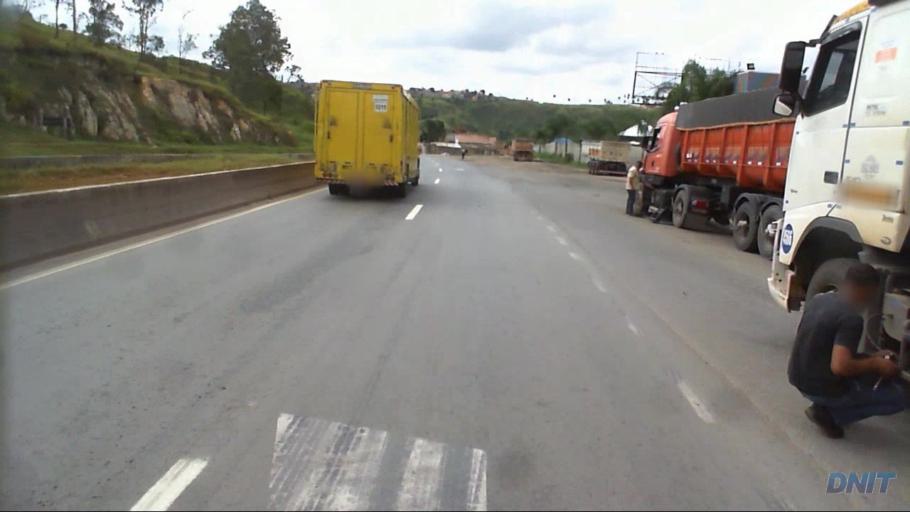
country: BR
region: Minas Gerais
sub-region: Santa Luzia
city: Santa Luzia
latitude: -19.8433
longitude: -43.8857
